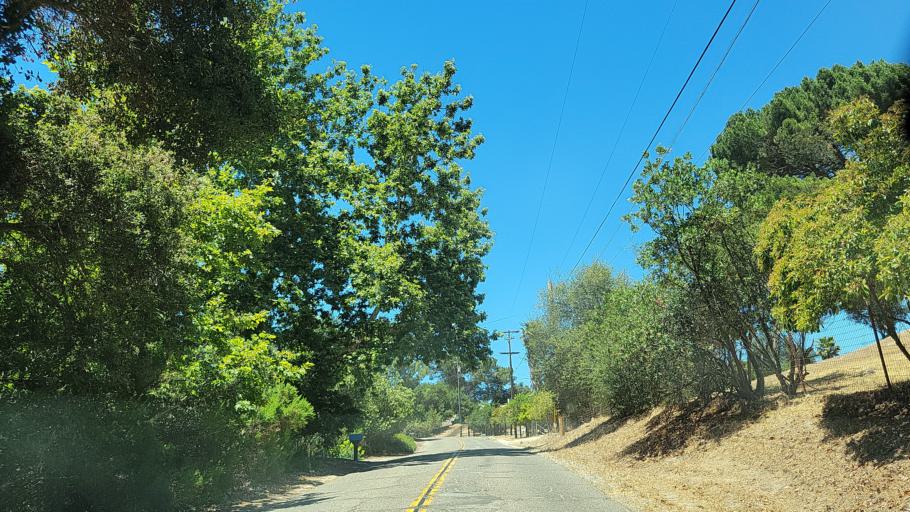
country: US
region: California
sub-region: San Luis Obispo County
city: Atascadero
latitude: 35.5058
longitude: -120.6772
